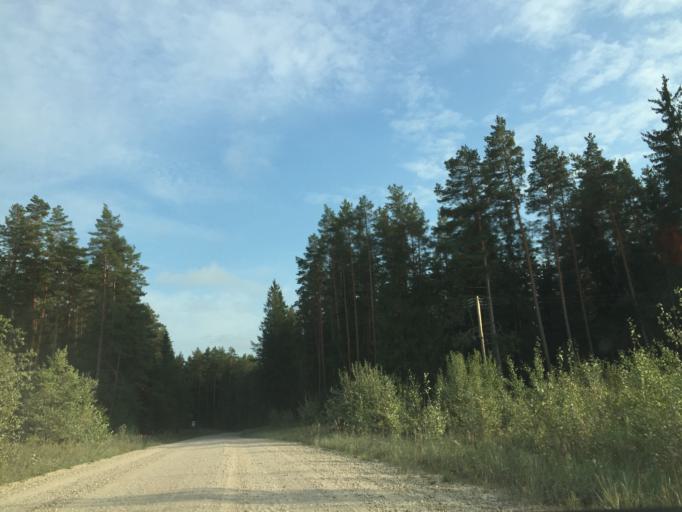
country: LV
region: Baldone
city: Baldone
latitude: 56.7901
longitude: 24.4415
